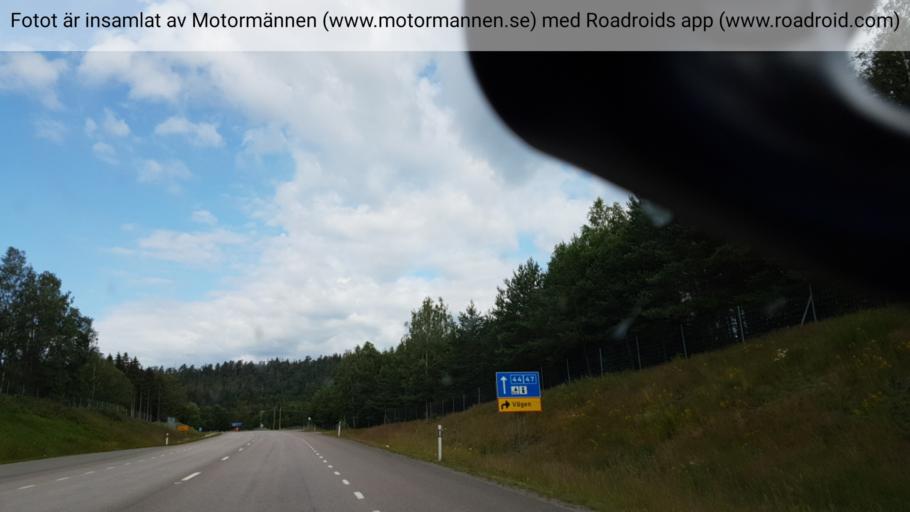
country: SE
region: Vaestra Goetaland
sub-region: Vanersborgs Kommun
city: Vargon
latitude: 58.3029
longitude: 12.5305
